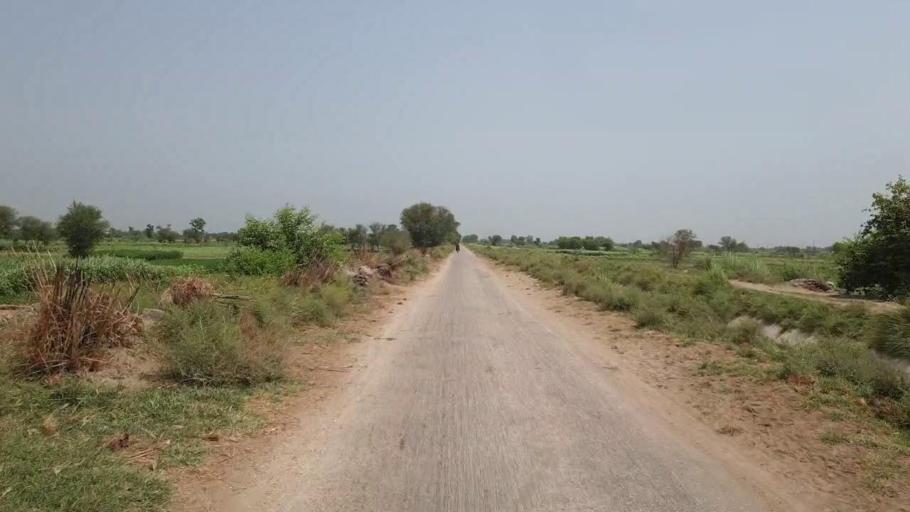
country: PK
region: Sindh
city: Nawabshah
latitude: 26.2745
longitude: 68.3142
